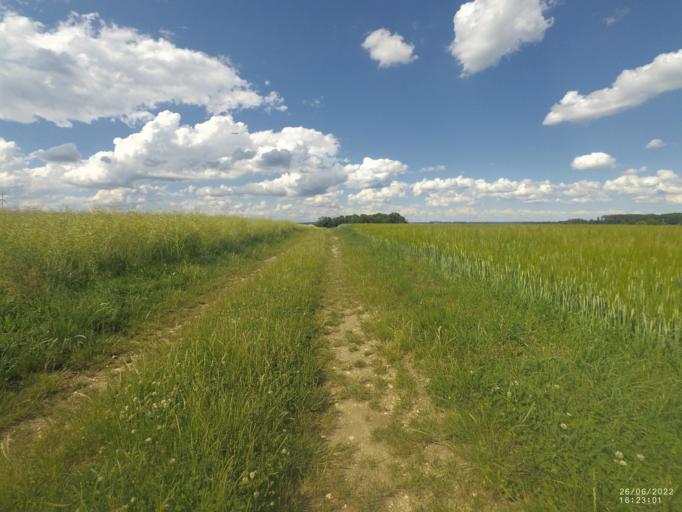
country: DE
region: Baden-Wuerttemberg
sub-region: Regierungsbezirk Stuttgart
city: Bohmenkirch
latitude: 48.6465
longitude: 9.9570
